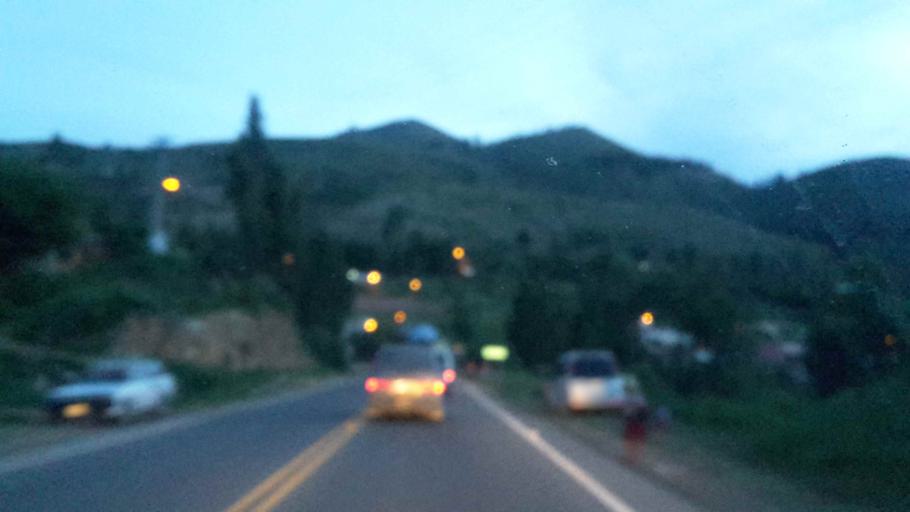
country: BO
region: Cochabamba
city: Colomi
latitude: -17.4167
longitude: -65.9420
